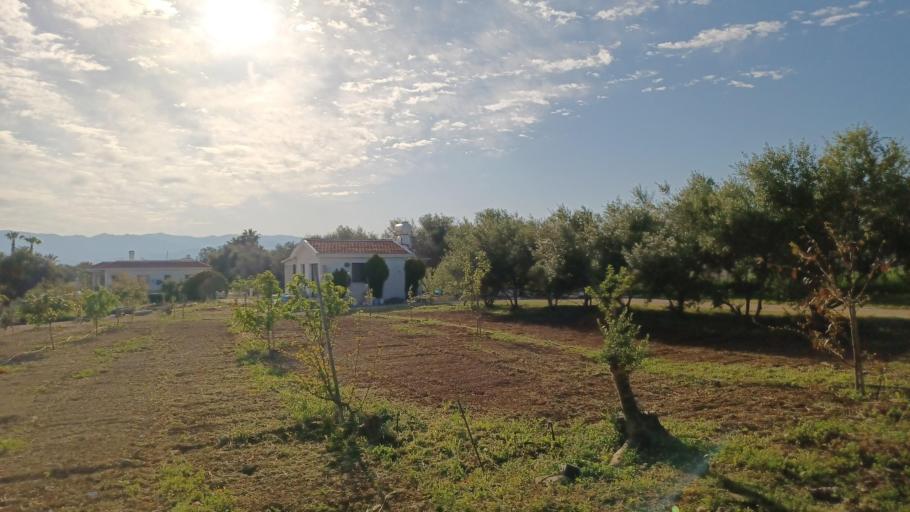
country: CY
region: Pafos
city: Polis
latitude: 35.0362
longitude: 32.3822
